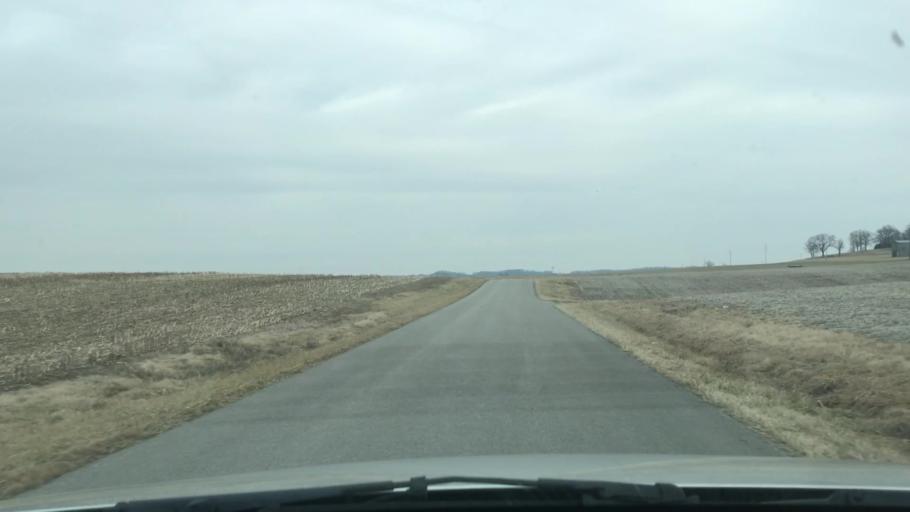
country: US
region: Kentucky
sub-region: Edmonson County
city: Brownsville
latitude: 37.0515
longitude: -86.2406
